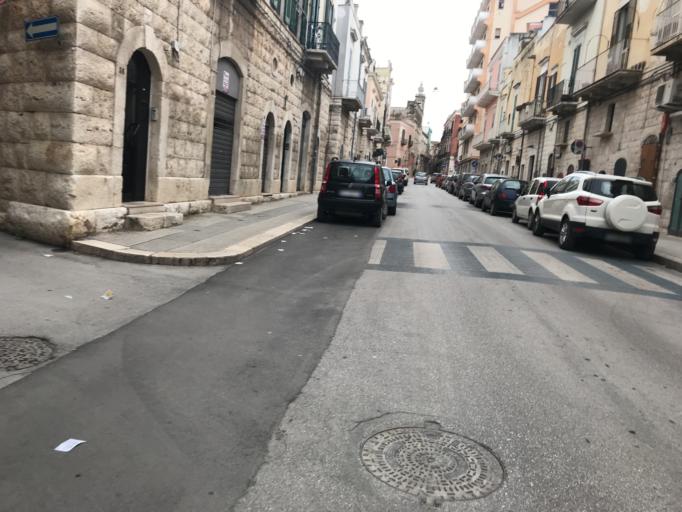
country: IT
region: Apulia
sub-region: Provincia di Bari
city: Corato
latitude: 41.1554
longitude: 16.4116
